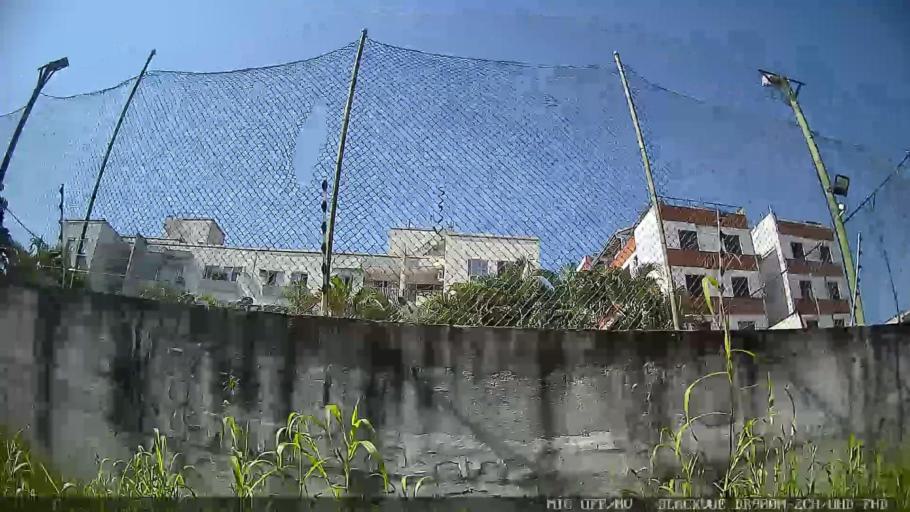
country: BR
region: Sao Paulo
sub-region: Guaruja
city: Guaruja
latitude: -24.0080
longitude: -46.2760
